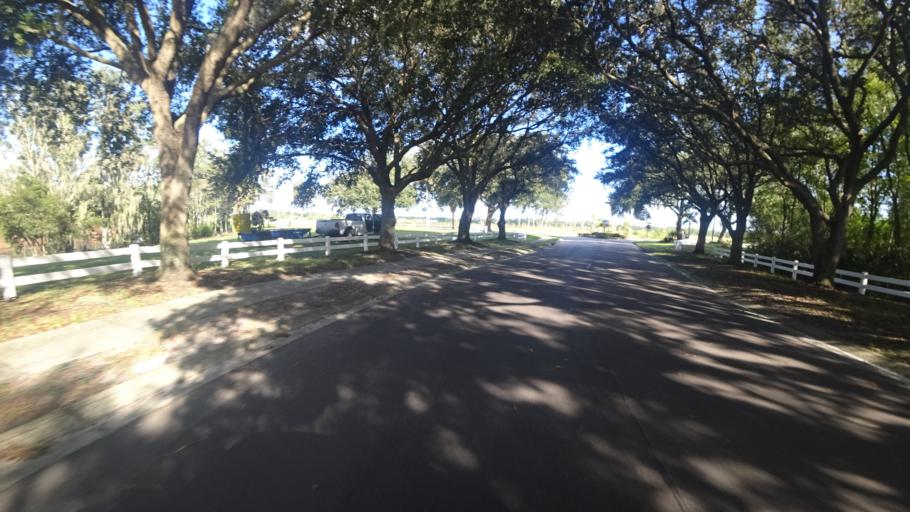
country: US
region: Florida
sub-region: Manatee County
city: Ellenton
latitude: 27.6005
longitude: -82.4929
